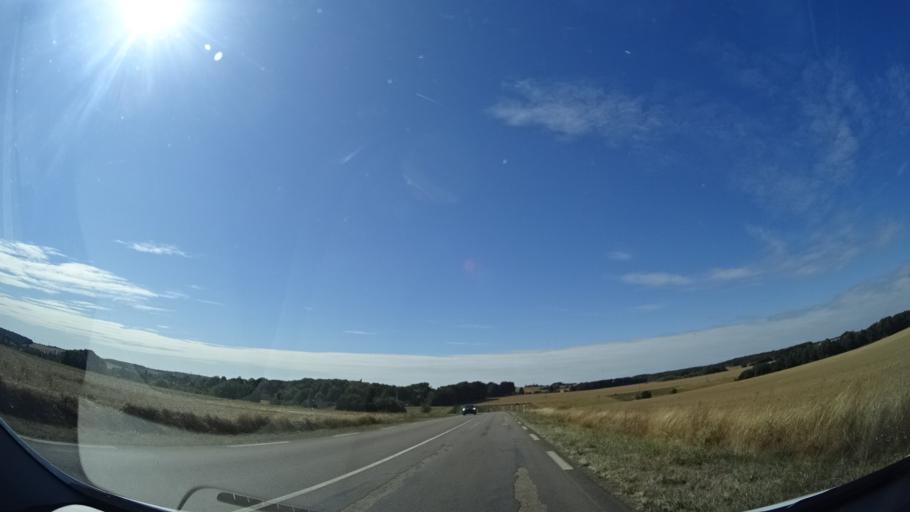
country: FR
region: Bourgogne
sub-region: Departement de l'Yonne
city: Charny
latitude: 47.9417
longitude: 3.1408
